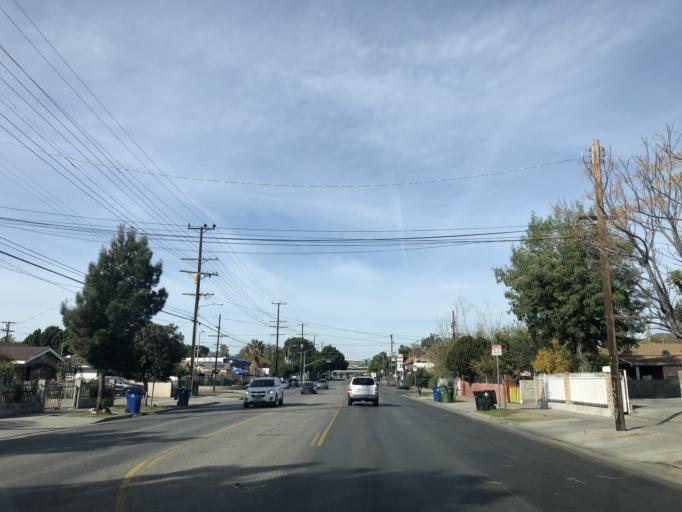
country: US
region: California
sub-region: Los Angeles County
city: San Fernando
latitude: 34.2632
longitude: -118.4370
